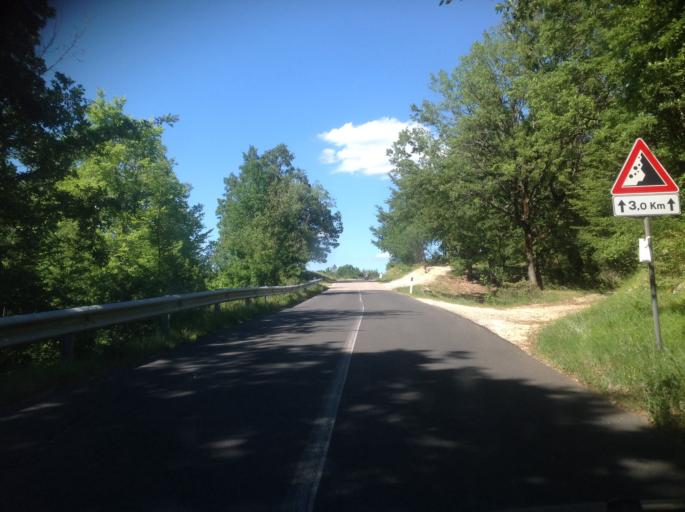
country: IT
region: Umbria
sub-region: Provincia di Terni
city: Stroncone
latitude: 42.4802
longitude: 12.6791
